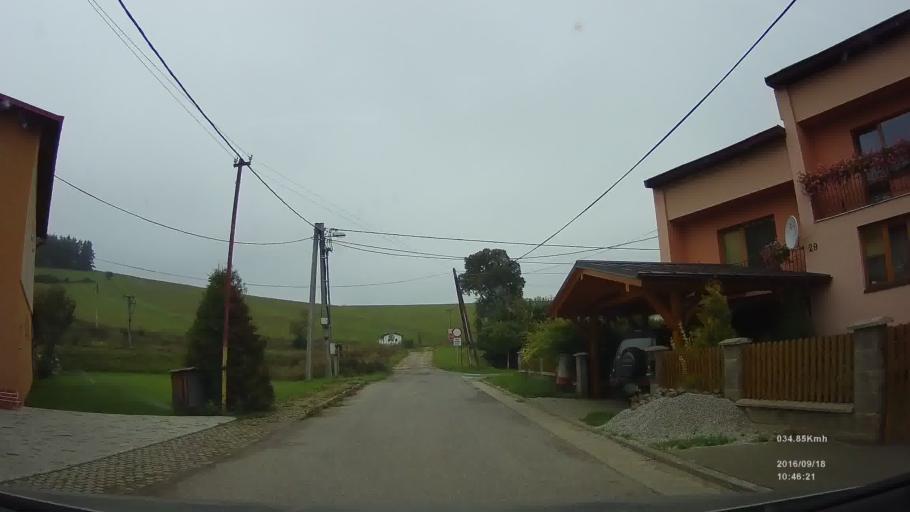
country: SK
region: Kosicky
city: Spisska Nova Ves
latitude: 48.9652
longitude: 20.5780
